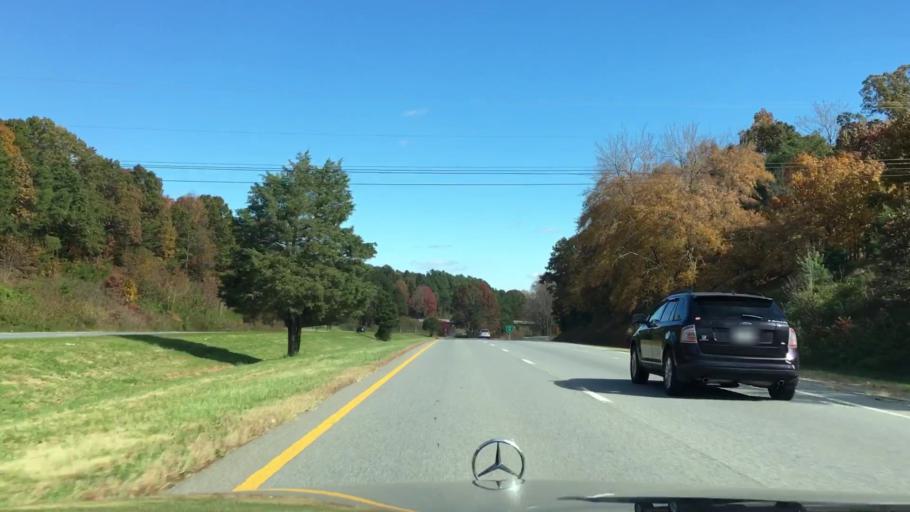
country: US
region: Virginia
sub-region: Campbell County
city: Altavista
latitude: 37.1338
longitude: -79.2950
